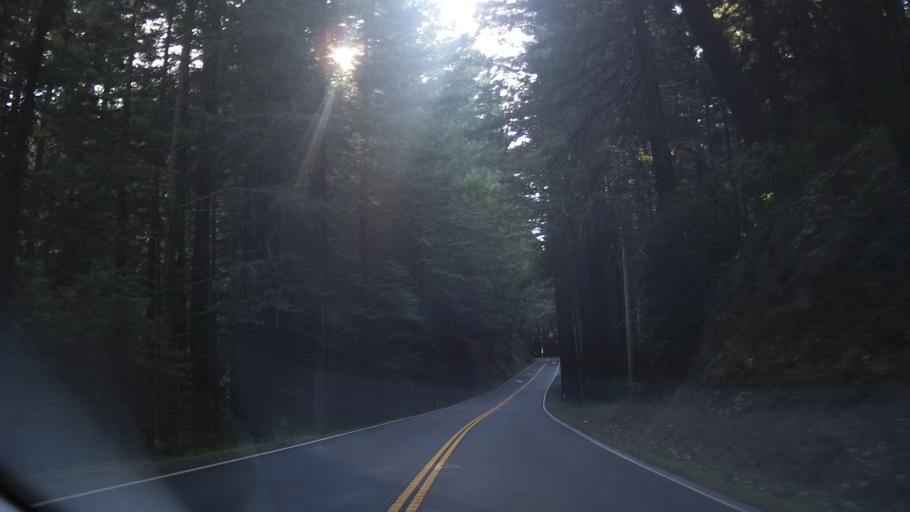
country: US
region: California
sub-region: Mendocino County
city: Brooktrails
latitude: 39.3469
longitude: -123.5663
